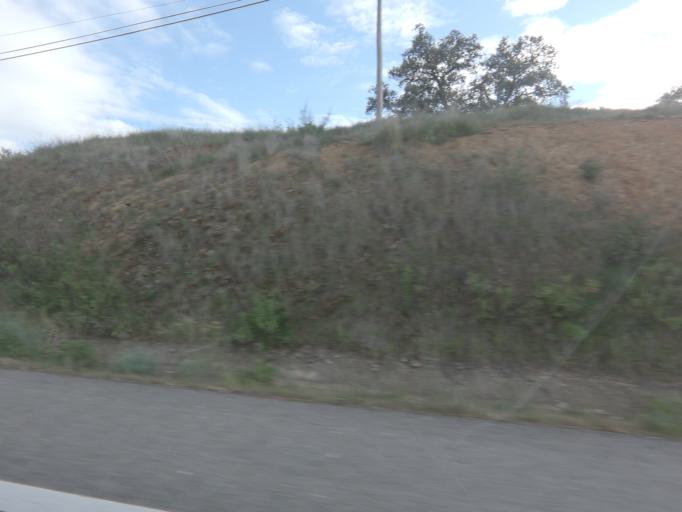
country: ES
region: Extremadura
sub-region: Provincia de Caceres
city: Canaveral
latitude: 39.8248
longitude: -6.3729
